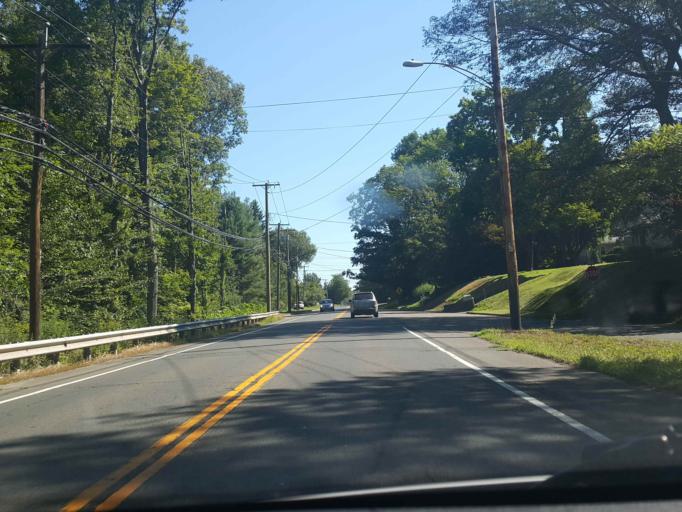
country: US
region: Connecticut
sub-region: New Haven County
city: North Branford
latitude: 41.3382
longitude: -72.7533
